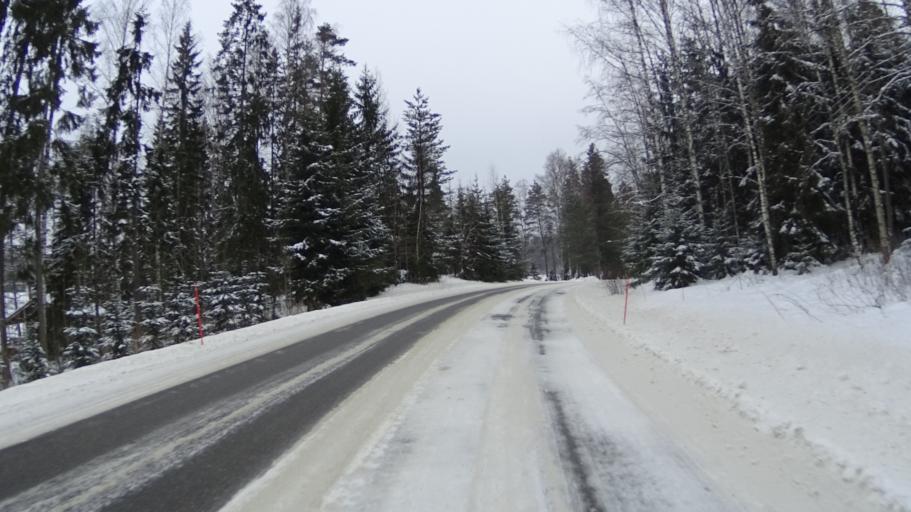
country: FI
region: Uusimaa
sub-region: Helsinki
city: Karkkila
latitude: 60.5035
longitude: 24.1400
